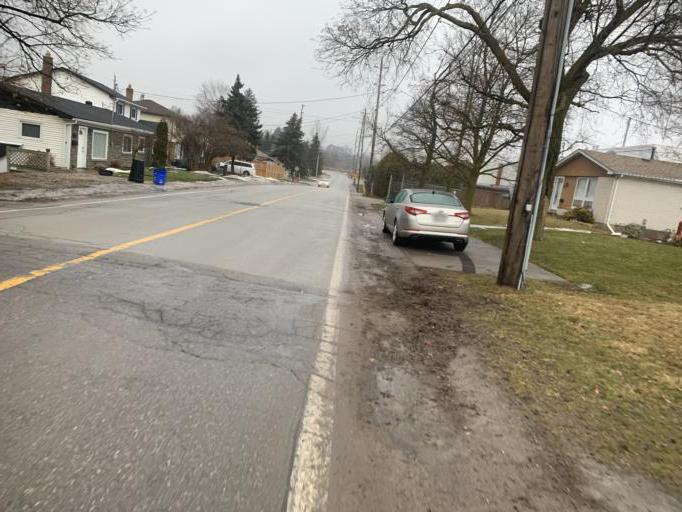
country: CA
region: Ontario
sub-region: Halton
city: Milton
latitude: 43.6572
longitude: -79.9242
